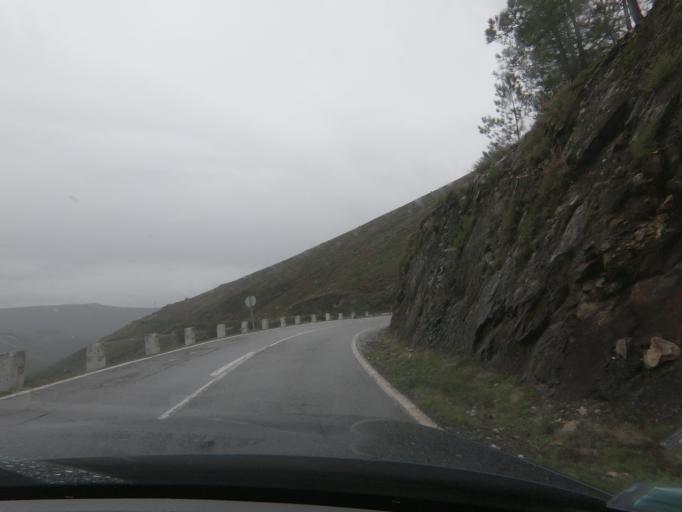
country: PT
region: Vila Real
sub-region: Mondim de Basto
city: Mondim de Basto
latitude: 41.3510
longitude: -7.8783
